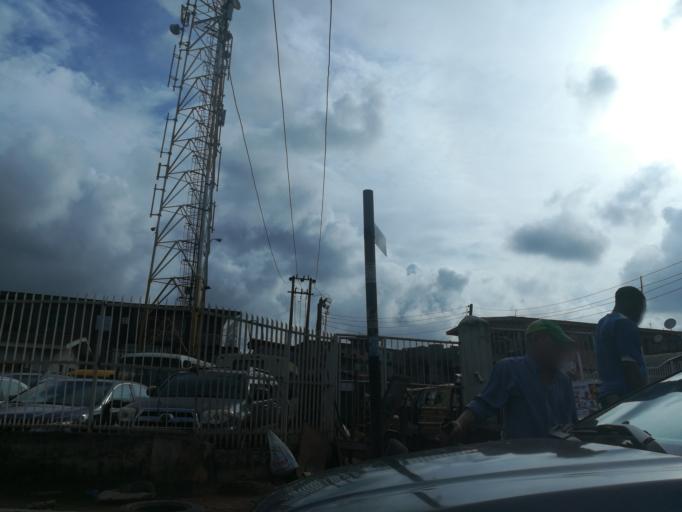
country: NG
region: Lagos
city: Somolu
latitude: 6.5421
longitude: 3.3787
